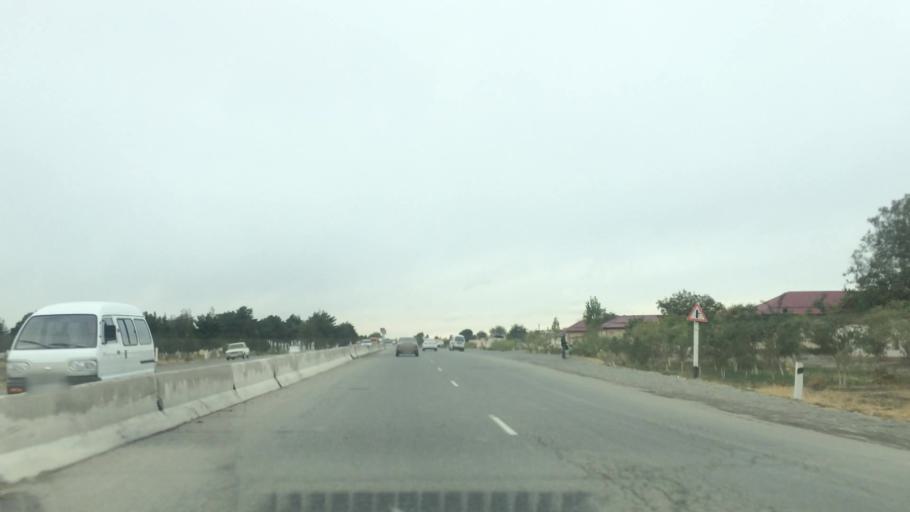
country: UZ
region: Samarqand
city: Jomboy
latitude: 39.7261
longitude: 67.1396
